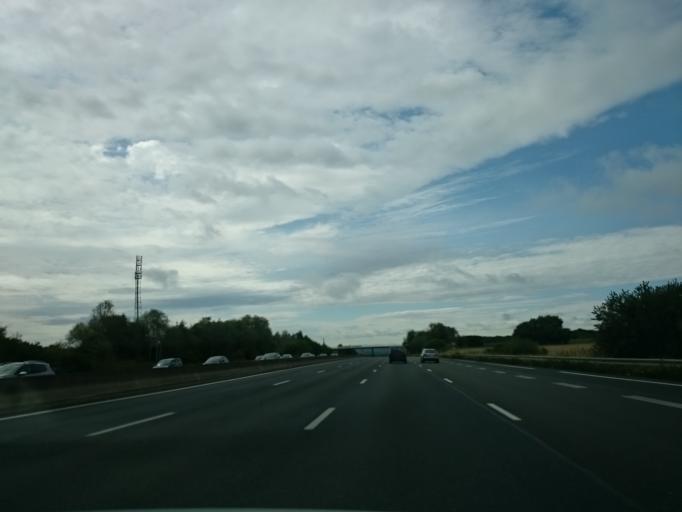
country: FR
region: Ile-de-France
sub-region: Departement de l'Essonne
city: Fontenay-les-Briis
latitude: 48.6323
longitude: 2.1442
